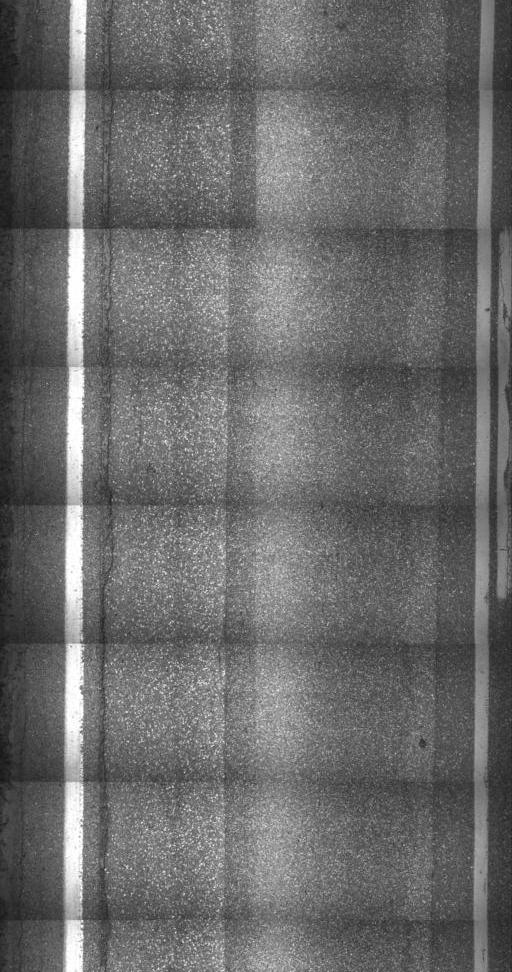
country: US
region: Vermont
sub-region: Washington County
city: Waterbury
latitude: 44.3193
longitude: -72.7312
